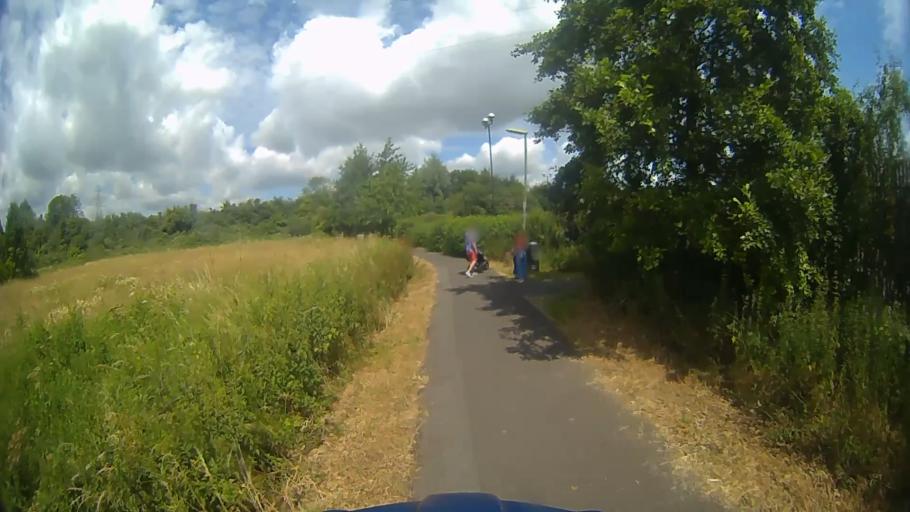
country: GB
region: England
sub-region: Hampshire
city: Andover
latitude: 51.2172
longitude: -1.4792
